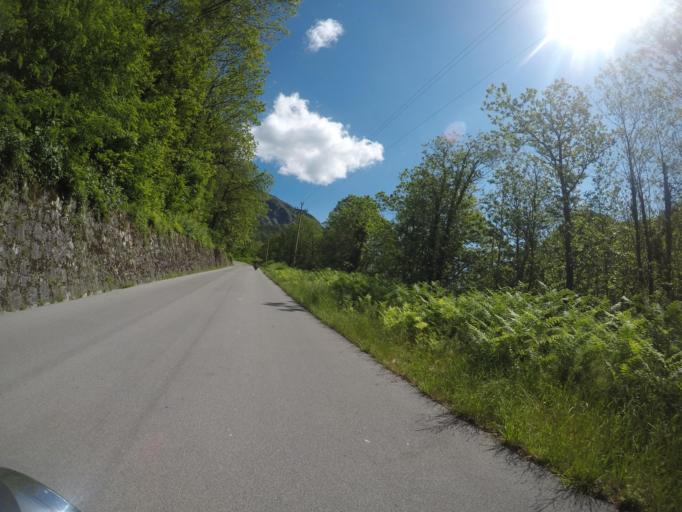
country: IT
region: Tuscany
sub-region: Provincia di Lucca
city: Fontana delle Monache
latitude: 44.0619
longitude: 10.3076
